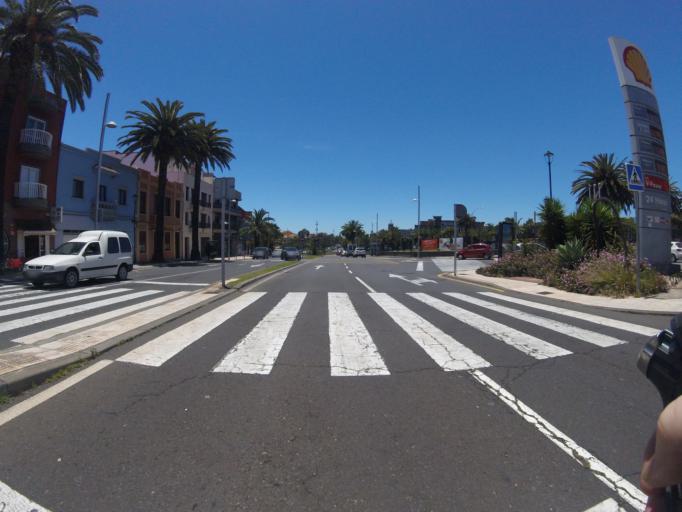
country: ES
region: Canary Islands
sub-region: Provincia de Santa Cruz de Tenerife
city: La Laguna
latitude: 28.4815
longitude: -16.3133
